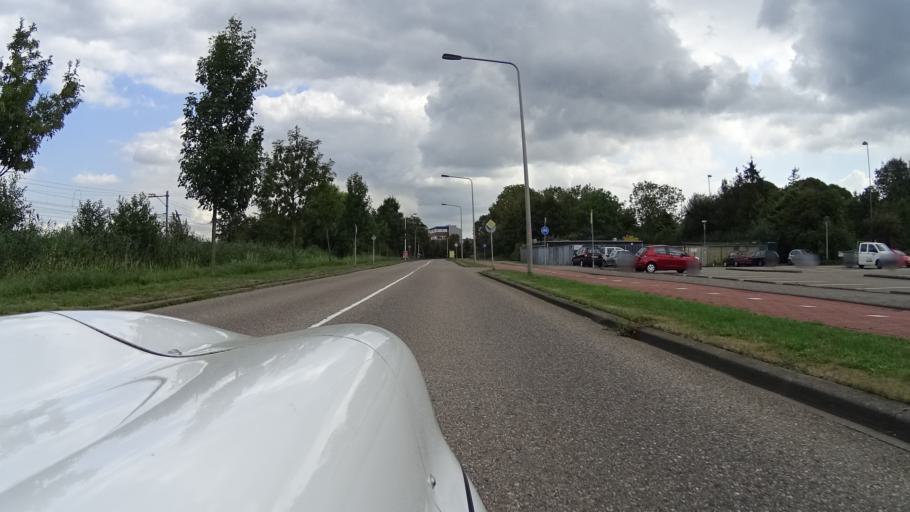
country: NL
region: South Holland
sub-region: Gemeente Sliedrecht
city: Sliedrecht
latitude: 51.8283
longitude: 4.7913
